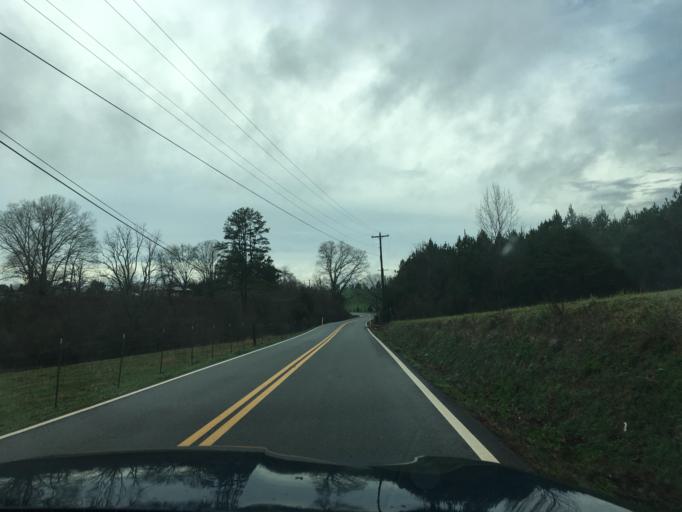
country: US
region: Tennessee
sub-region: McMinn County
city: Englewood
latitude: 35.4166
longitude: -84.4625
